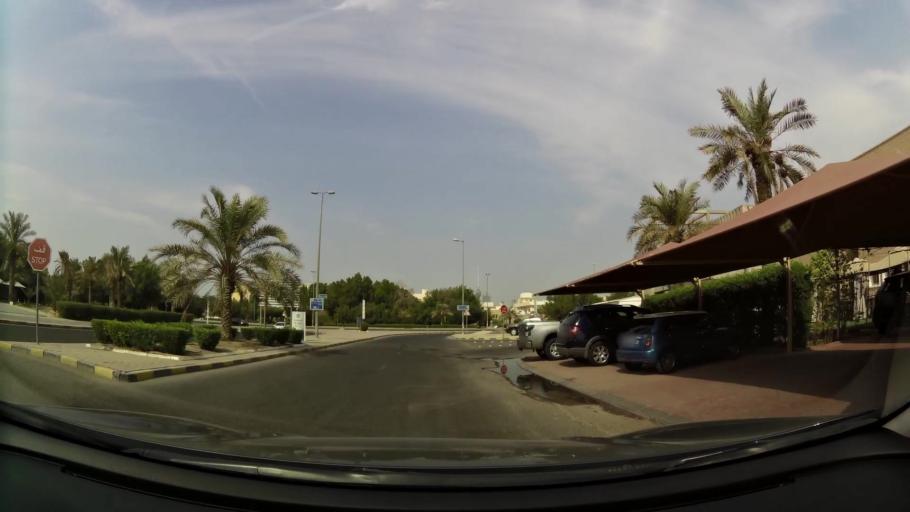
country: KW
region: Al Asimah
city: Ash Shamiyah
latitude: 29.3432
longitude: 47.9758
